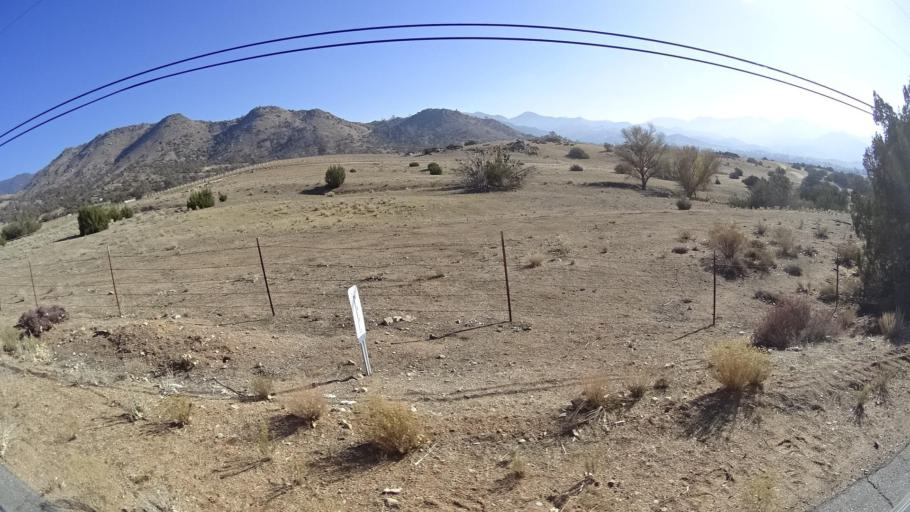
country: US
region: California
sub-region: Kern County
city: Tehachapi
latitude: 35.3536
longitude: -118.3838
